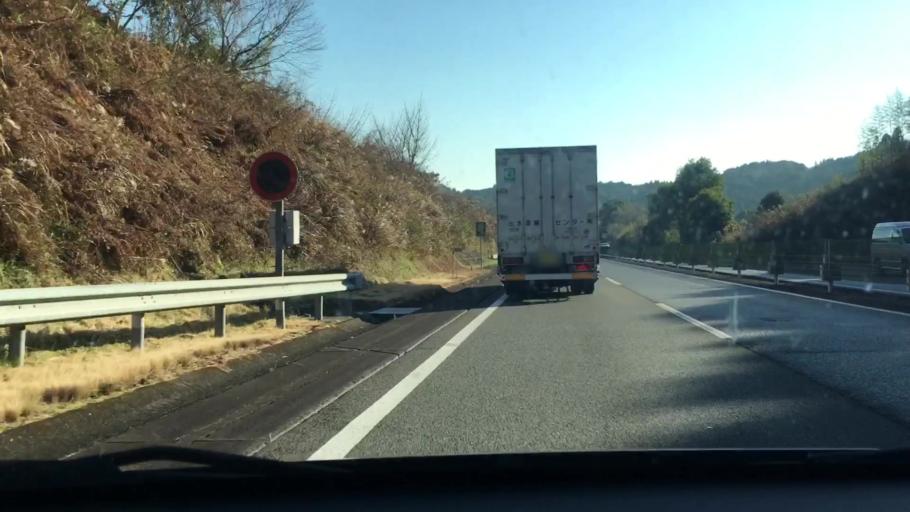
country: JP
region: Kagoshima
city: Kajiki
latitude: 31.8825
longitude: 130.6954
